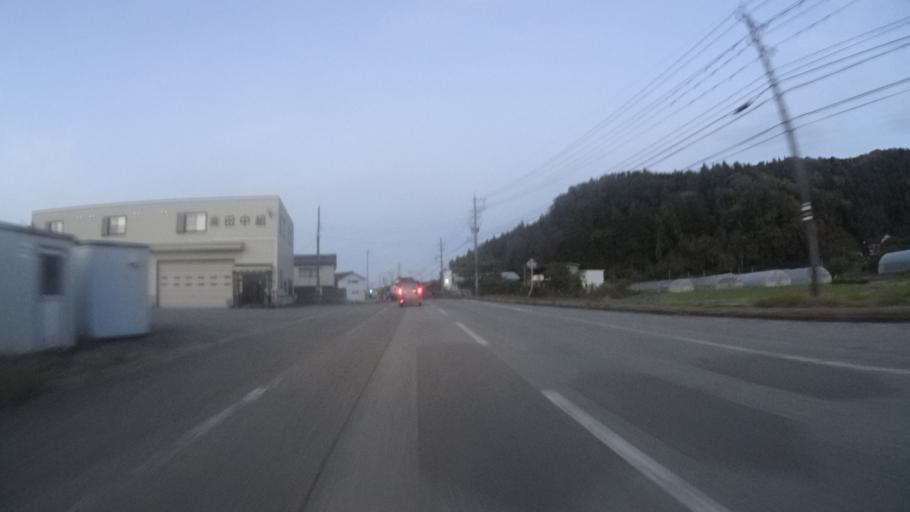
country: JP
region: Ishikawa
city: Nanao
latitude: 37.3779
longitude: 136.8831
